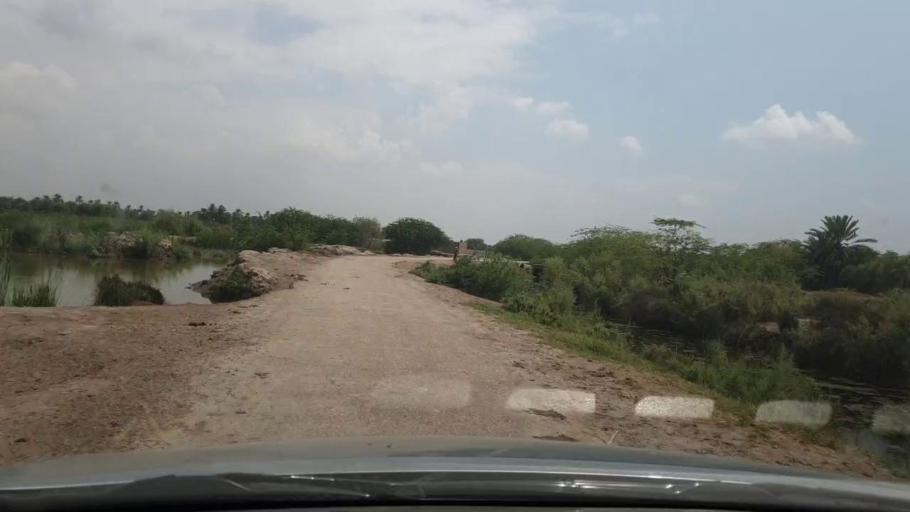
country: PK
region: Sindh
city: Kot Diji
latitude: 27.3832
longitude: 68.7143
